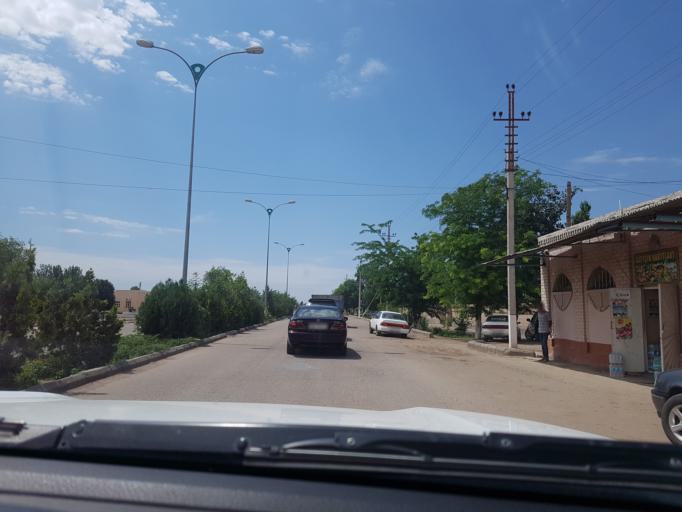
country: TM
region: Dasoguz
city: Koeneuergench
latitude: 42.3243
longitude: 59.1404
